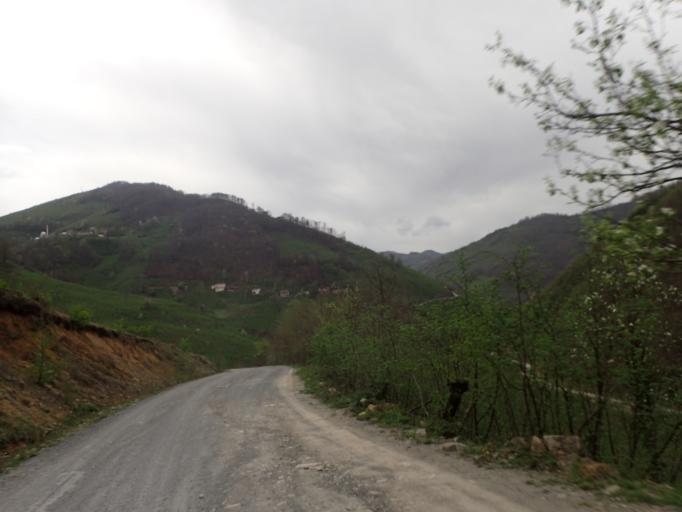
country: TR
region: Ordu
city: Korgan
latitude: 40.7694
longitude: 37.3325
